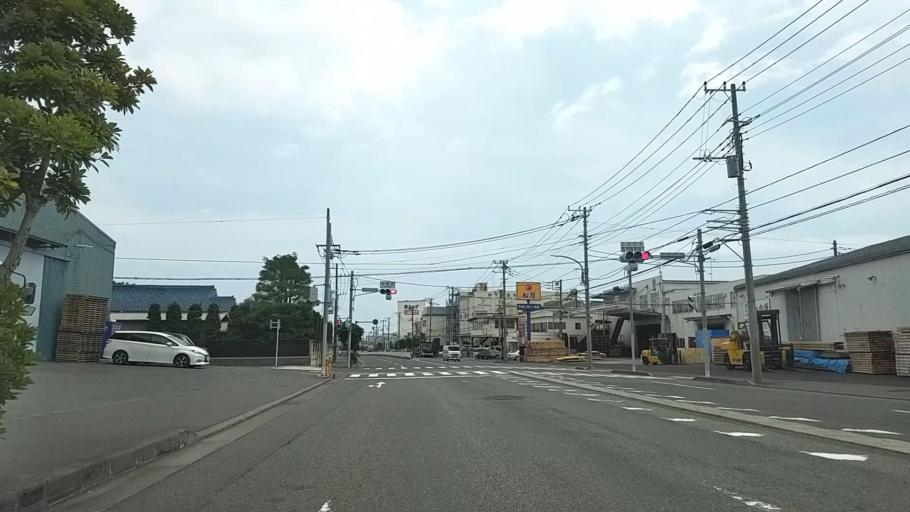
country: JP
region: Kanagawa
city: Minami-rinkan
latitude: 35.4530
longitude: 139.4179
